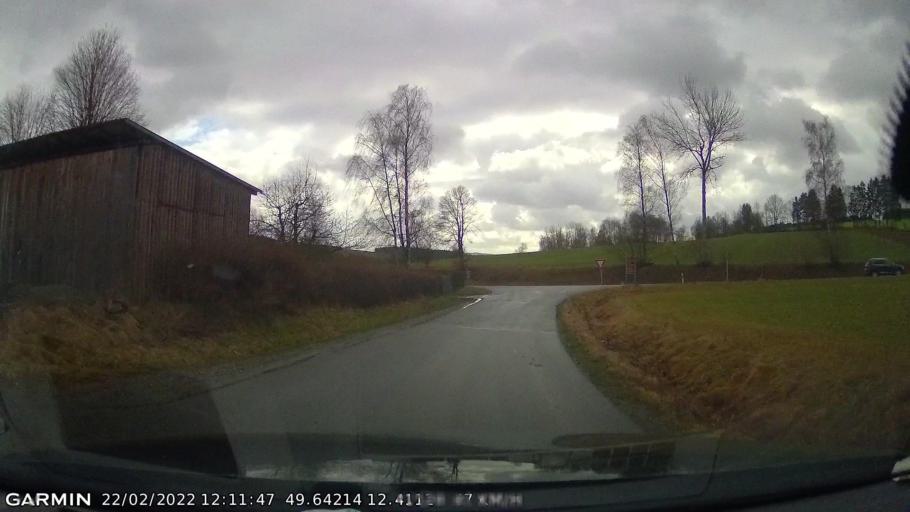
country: DE
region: Bavaria
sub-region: Upper Palatinate
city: Pleystein
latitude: 49.6420
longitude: 12.4110
